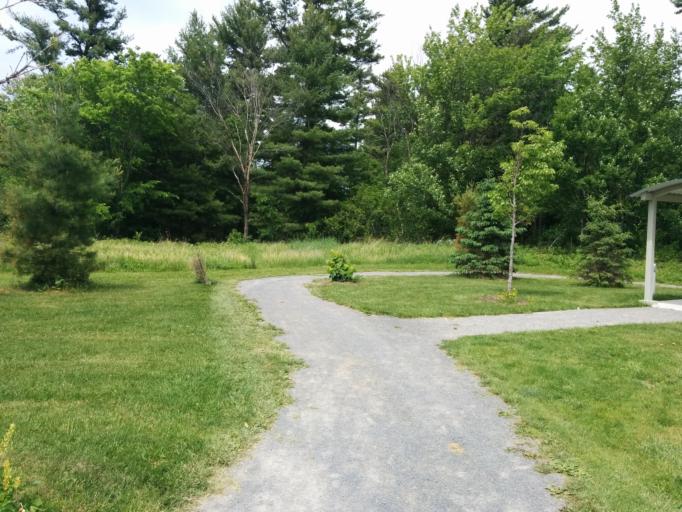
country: CA
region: Ontario
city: Clarence-Rockland
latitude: 45.4788
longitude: -75.4598
